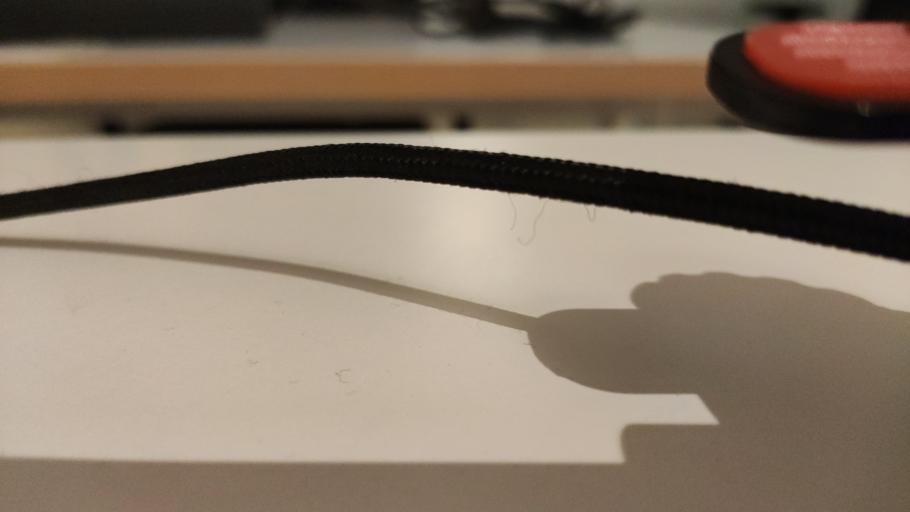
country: RU
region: Moskovskaya
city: Shemetovo
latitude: 56.4105
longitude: 37.9966
